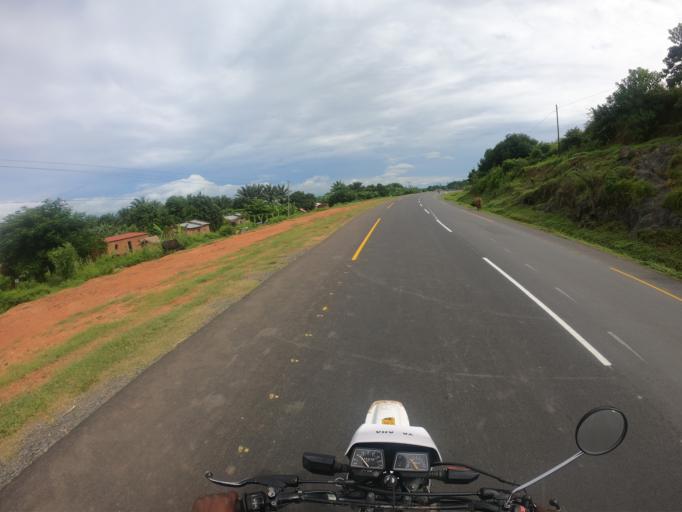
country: TZ
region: Mbeya
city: Kyela
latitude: -9.7067
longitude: 33.8660
